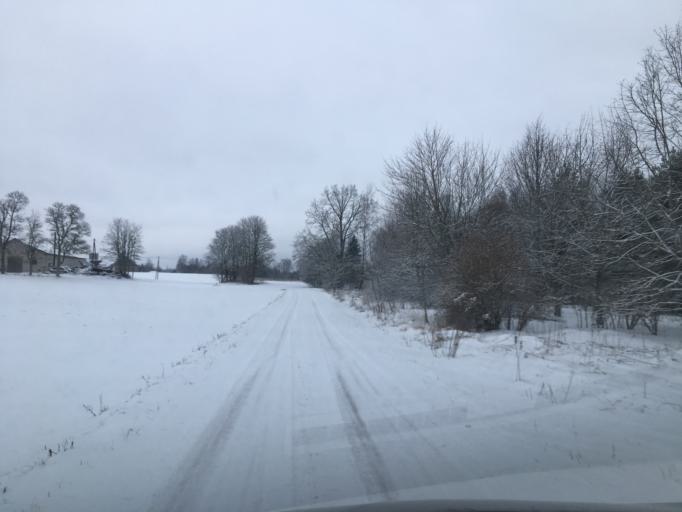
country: EE
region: Tartu
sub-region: Puhja vald
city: Puhja
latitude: 58.1925
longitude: 26.2001
